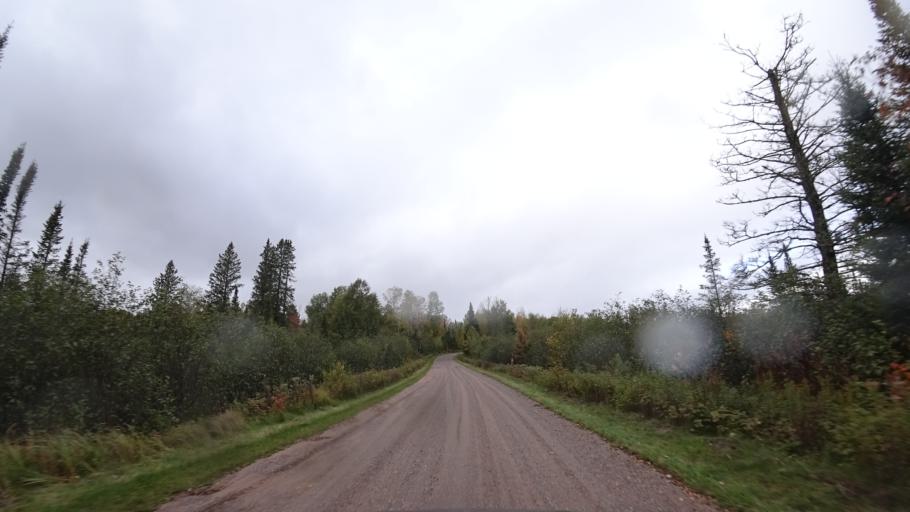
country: US
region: Wisconsin
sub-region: Sawyer County
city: Little Round Lake
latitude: 45.9811
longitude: -90.9970
